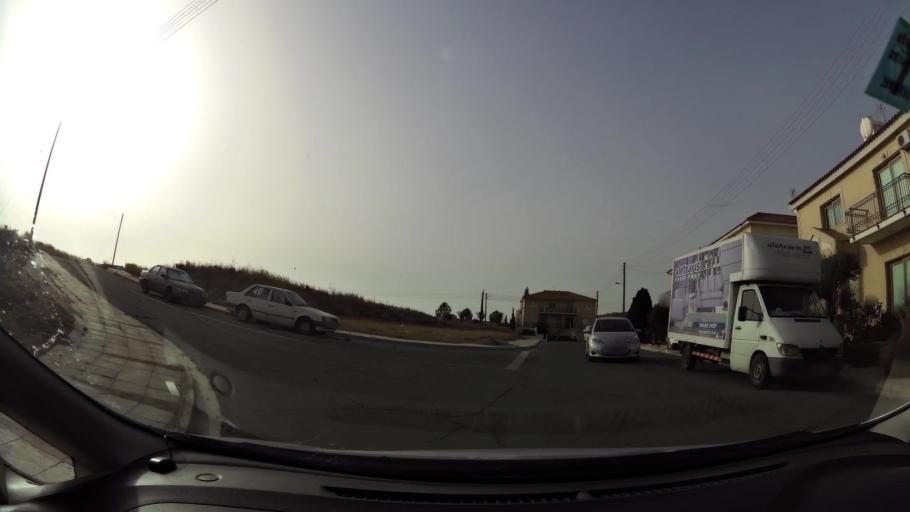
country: CY
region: Lefkosia
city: Dali
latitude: 35.0629
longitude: 33.3919
